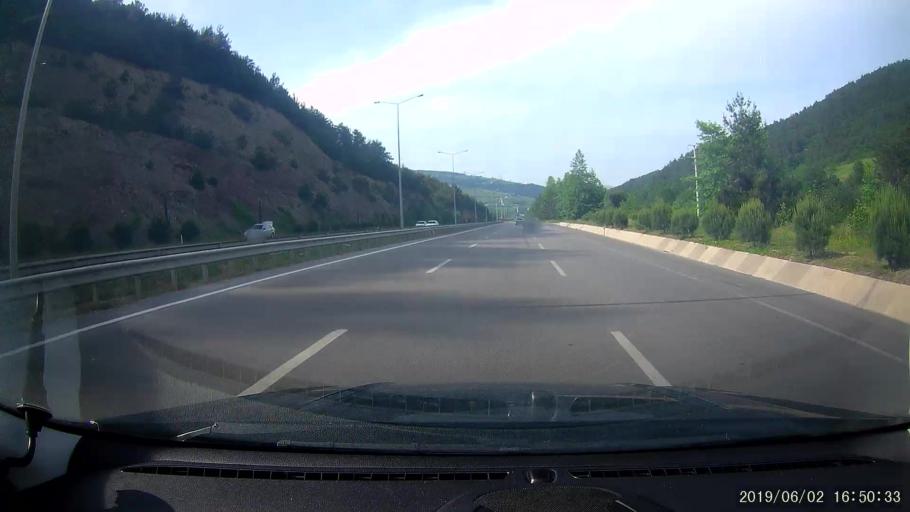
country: TR
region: Samsun
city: Samsun
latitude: 41.2569
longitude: 36.1739
